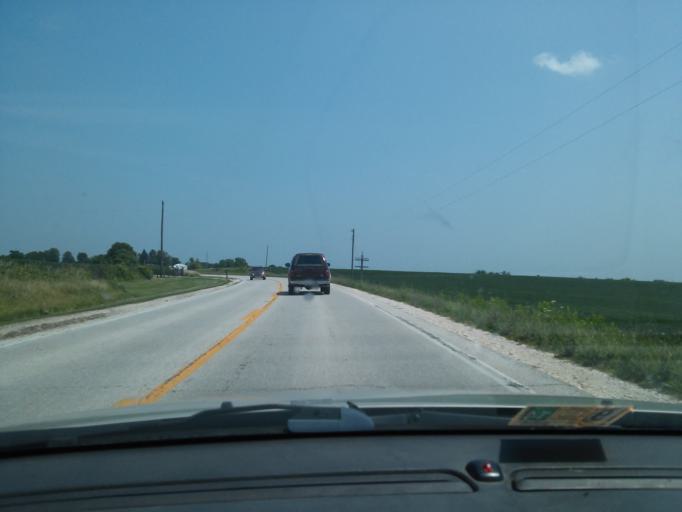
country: US
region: Illinois
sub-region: Pike County
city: Pittsfield
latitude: 39.5804
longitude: -90.9037
